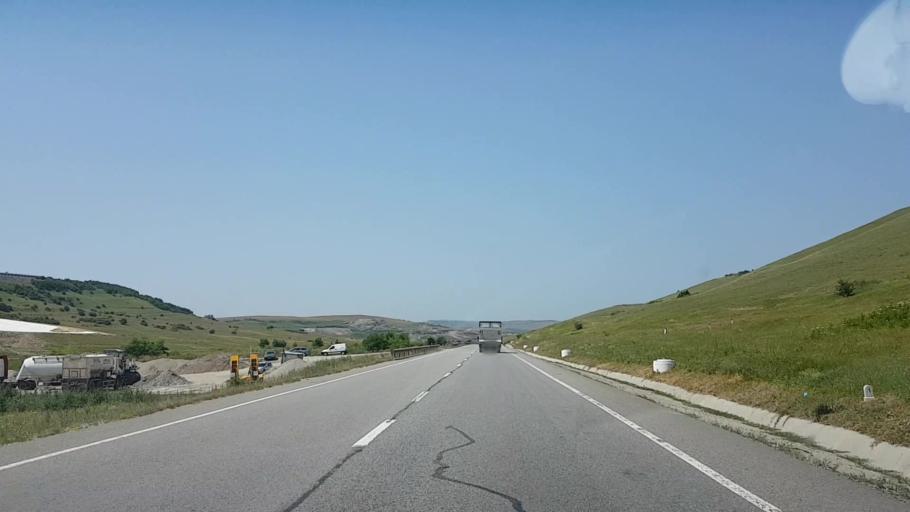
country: RO
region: Cluj
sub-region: Comuna Apahida
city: Dezmir
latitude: 46.7490
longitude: 23.7069
